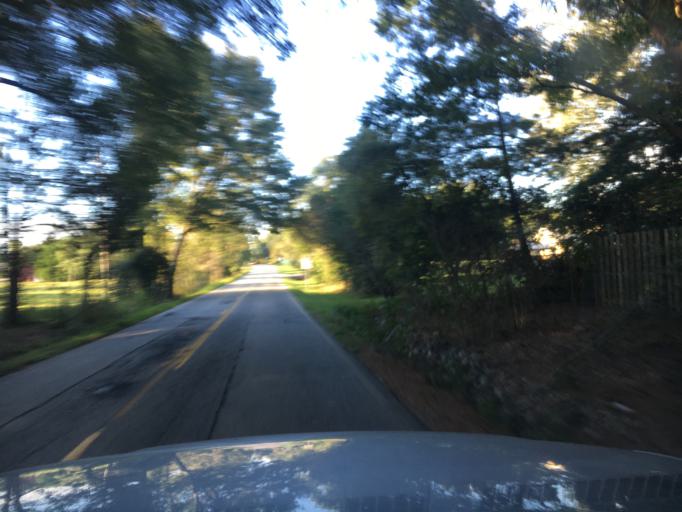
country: US
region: South Carolina
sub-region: Spartanburg County
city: Fairforest
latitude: 34.8865
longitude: -82.0480
